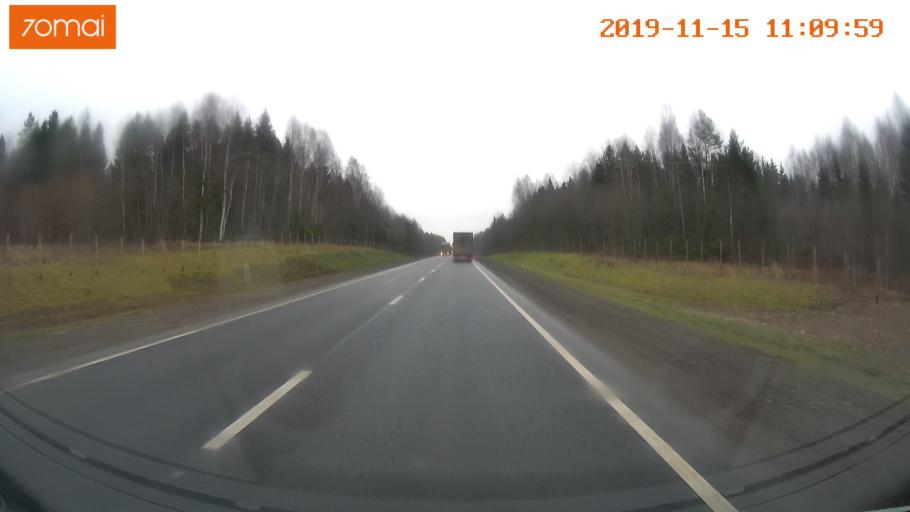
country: RU
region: Vologda
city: Chebsara
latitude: 59.1207
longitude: 39.1110
